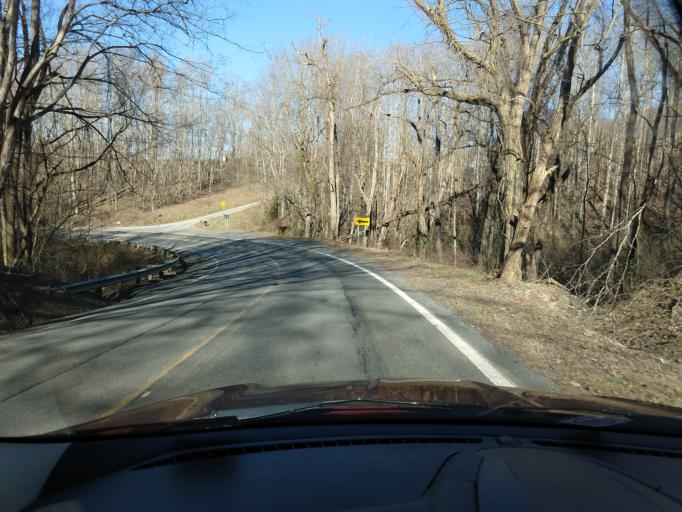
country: US
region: West Virginia
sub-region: Summers County
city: Hinton
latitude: 37.7604
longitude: -80.8913
